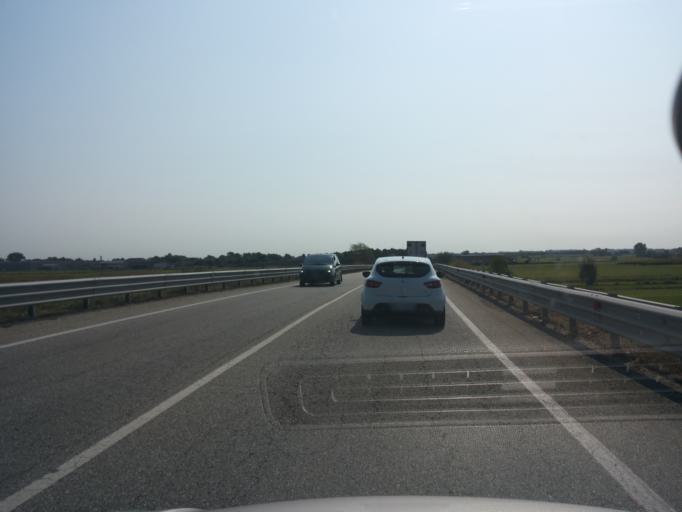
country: IT
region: Piedmont
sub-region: Provincia di Vercelli
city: Borgo Vercelli
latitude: 45.3648
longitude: 8.4679
